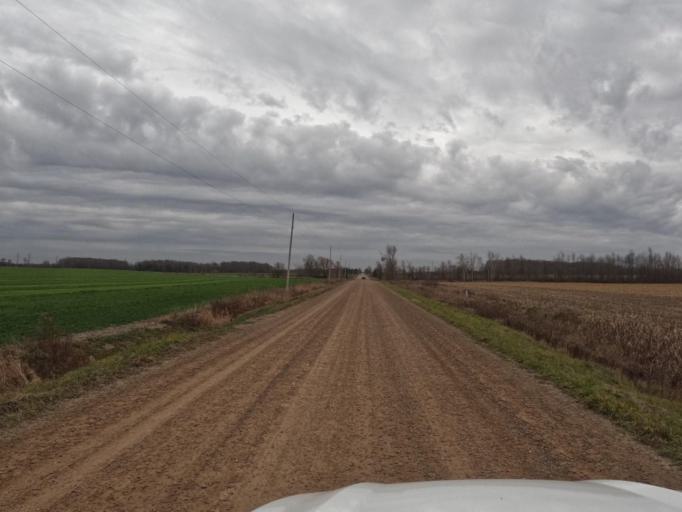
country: CA
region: Ontario
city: Shelburne
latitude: 43.9858
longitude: -80.3836
